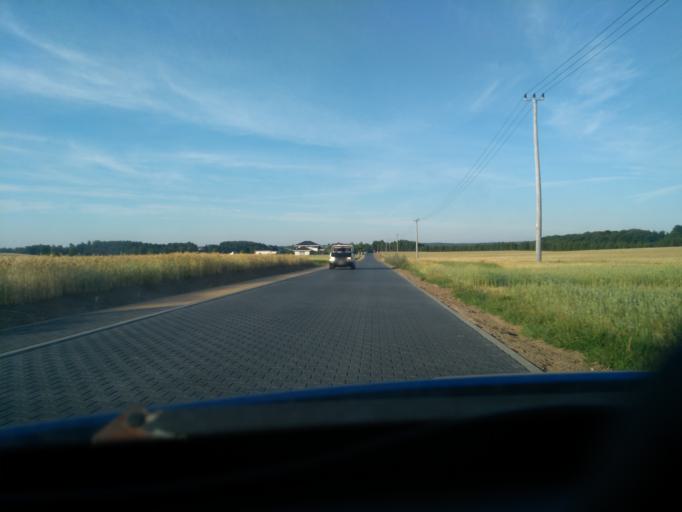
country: PL
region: Pomeranian Voivodeship
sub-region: Powiat kartuski
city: Przodkowo
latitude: 54.3894
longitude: 18.3213
